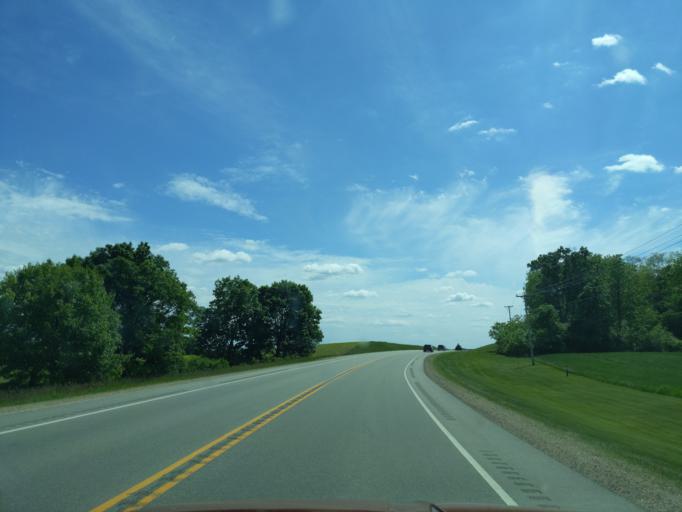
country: US
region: Wisconsin
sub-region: Columbia County
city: Pardeeville
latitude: 43.4710
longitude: -89.3151
